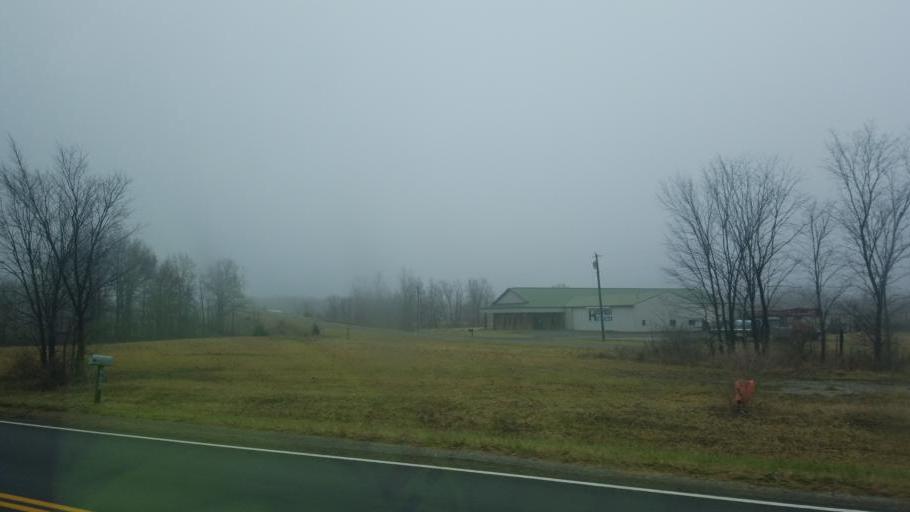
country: US
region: Ohio
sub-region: Union County
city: Marysville
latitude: 40.2606
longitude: -83.4592
